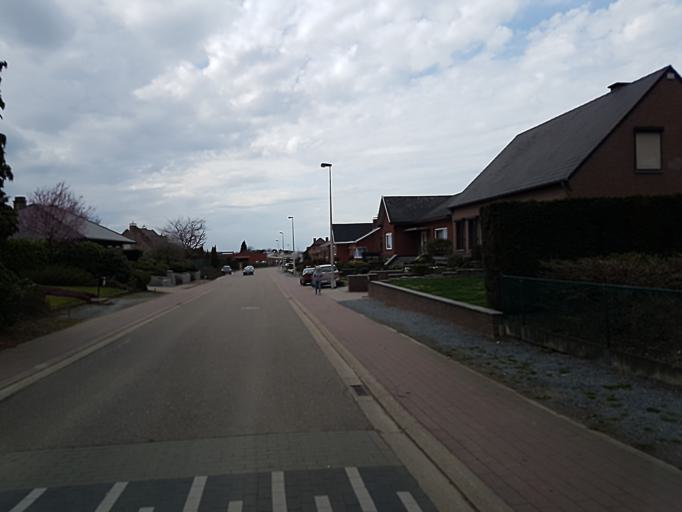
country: BE
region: Flanders
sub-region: Provincie Limburg
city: Nieuwerkerken
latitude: 50.8807
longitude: 5.2332
